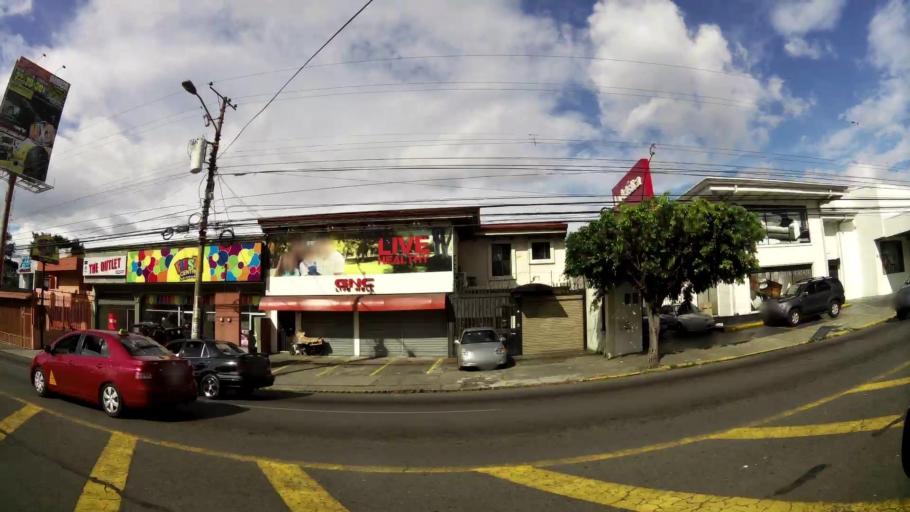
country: CR
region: San Jose
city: San Rafael
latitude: 9.9383
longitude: -84.1160
